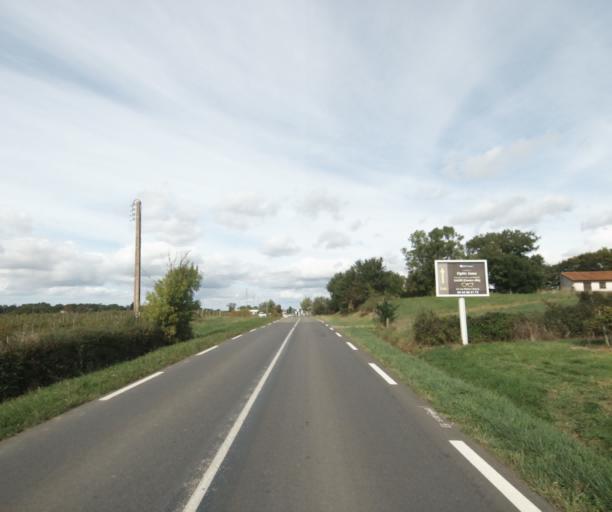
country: FR
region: Midi-Pyrenees
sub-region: Departement du Gers
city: Eauze
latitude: 43.8365
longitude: 0.0925
